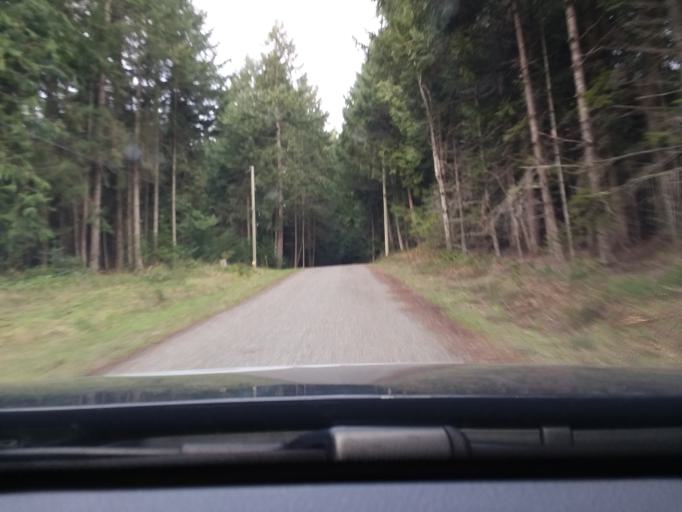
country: CA
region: British Columbia
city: North Saanich
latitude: 48.8743
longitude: -123.3302
